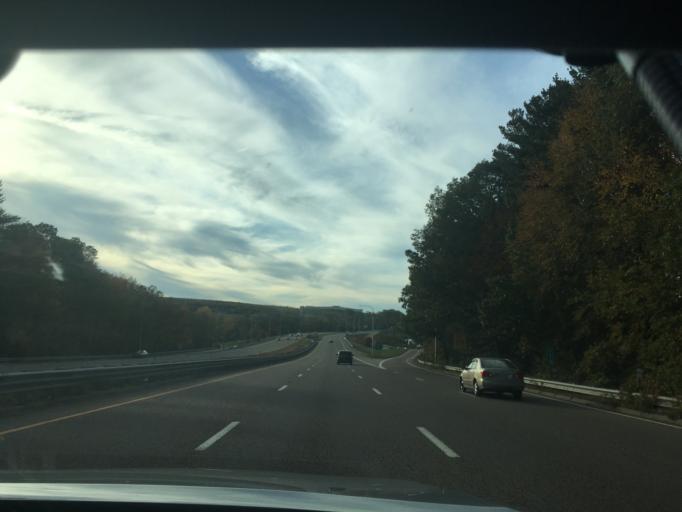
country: US
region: Rhode Island
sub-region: Providence County
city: Johnston
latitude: 41.8169
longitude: -71.4922
